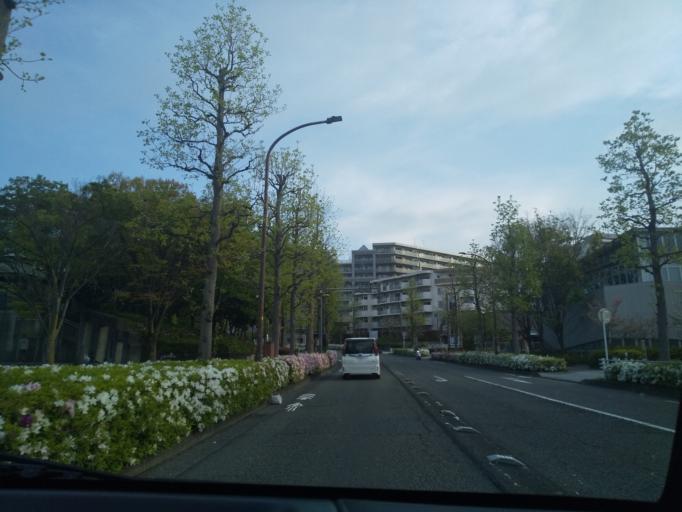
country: JP
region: Tokyo
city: Chofugaoka
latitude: 35.6411
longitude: 139.4899
